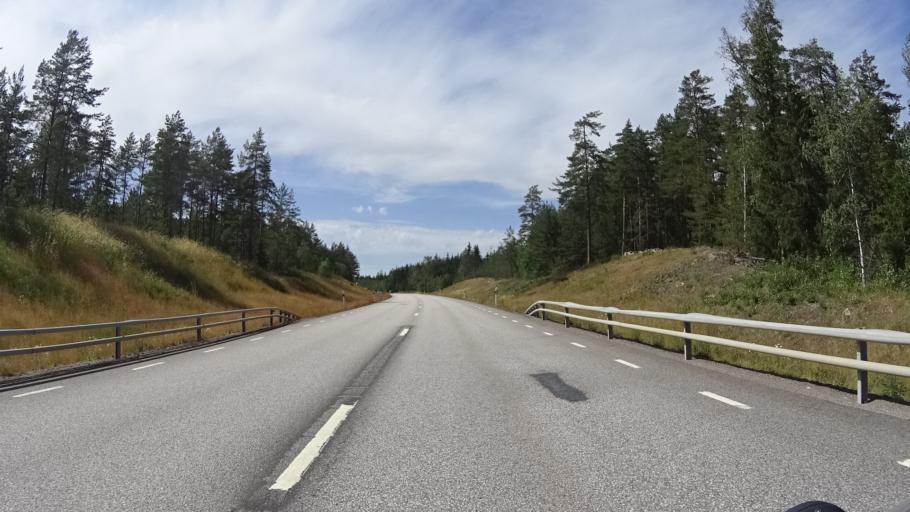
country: SE
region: Kalmar
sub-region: Vasterviks Kommun
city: Overum
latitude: 57.9582
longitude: 16.3703
